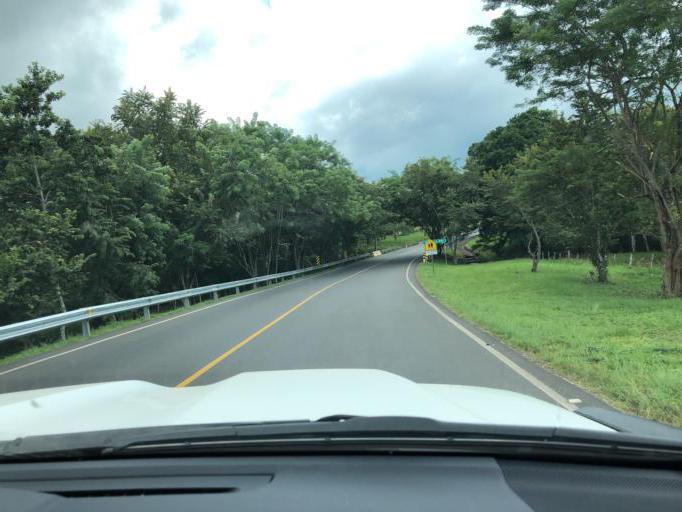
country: NI
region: Chontales
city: Santo Tomas
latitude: 12.0627
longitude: -85.0549
